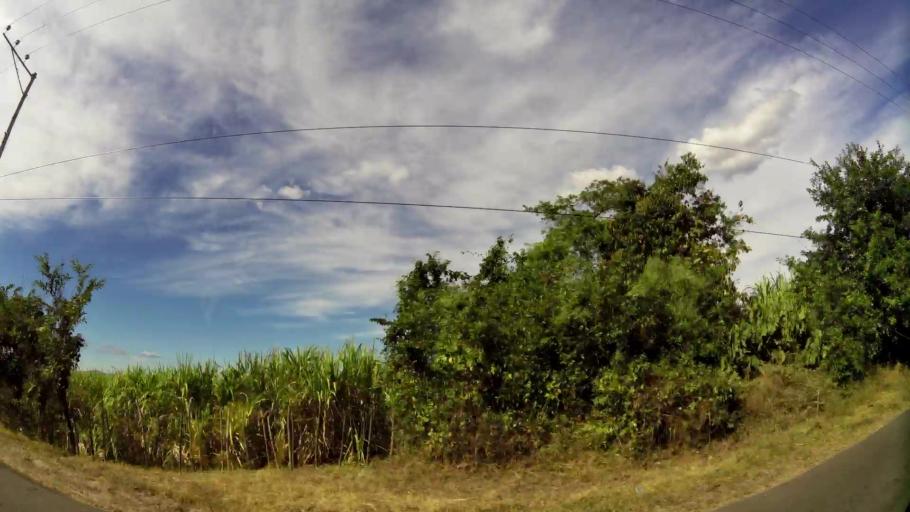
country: SV
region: San Salvador
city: Aguilares
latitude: 13.9638
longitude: -89.1205
